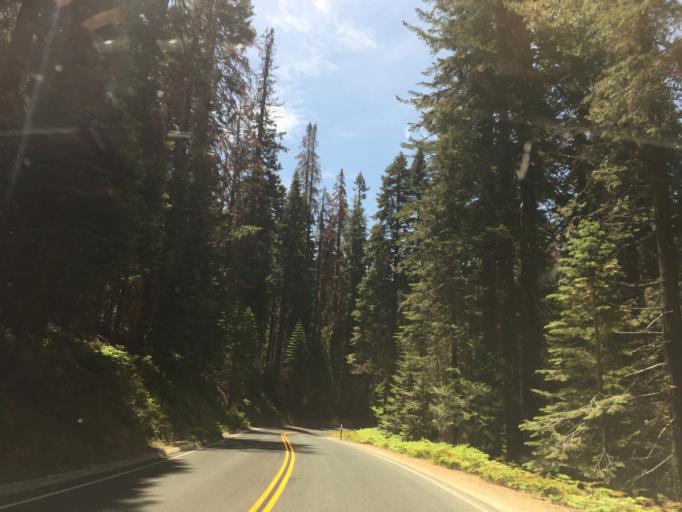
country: US
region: California
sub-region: Fresno County
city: Squaw Valley
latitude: 36.7535
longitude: -118.9598
